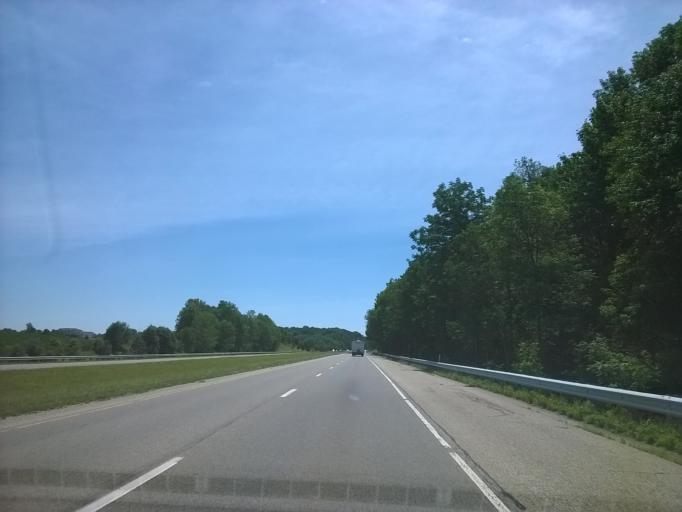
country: US
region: Indiana
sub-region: Decatur County
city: Greensburg
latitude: 39.3376
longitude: -85.4086
